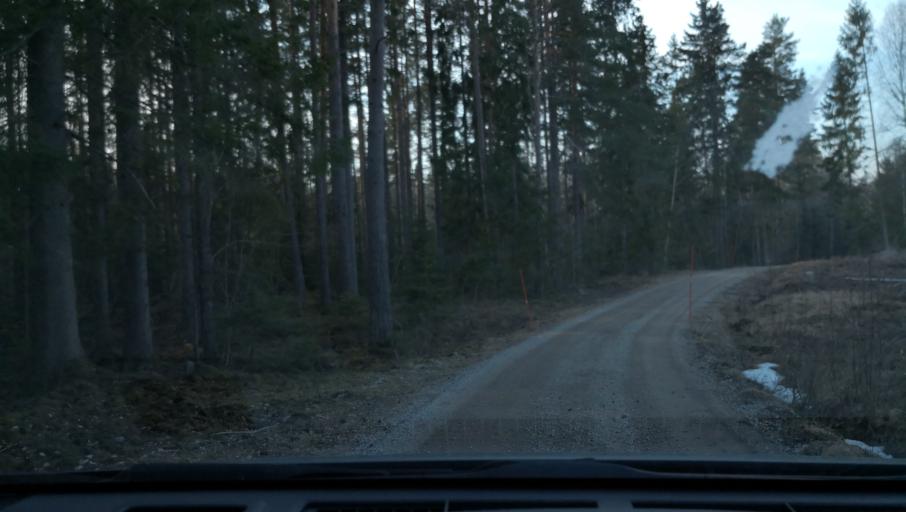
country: SE
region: OErebro
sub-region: Lindesbergs Kommun
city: Frovi
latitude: 59.3885
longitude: 15.3557
